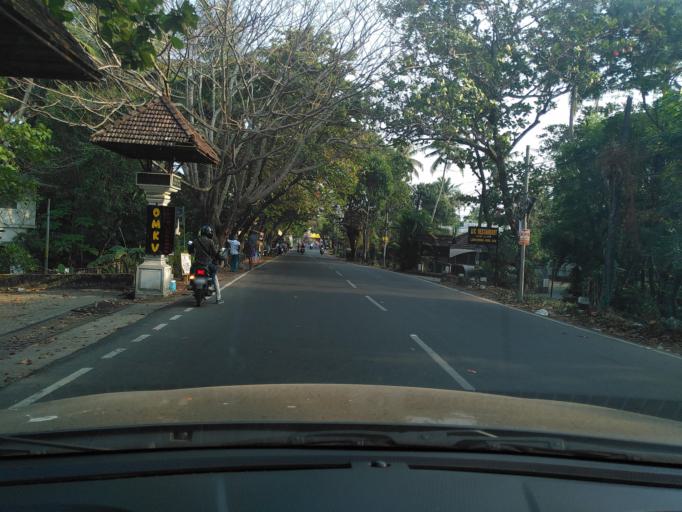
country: IN
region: Kerala
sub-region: Ernakulam
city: Cochin
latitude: 9.8991
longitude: 76.2833
